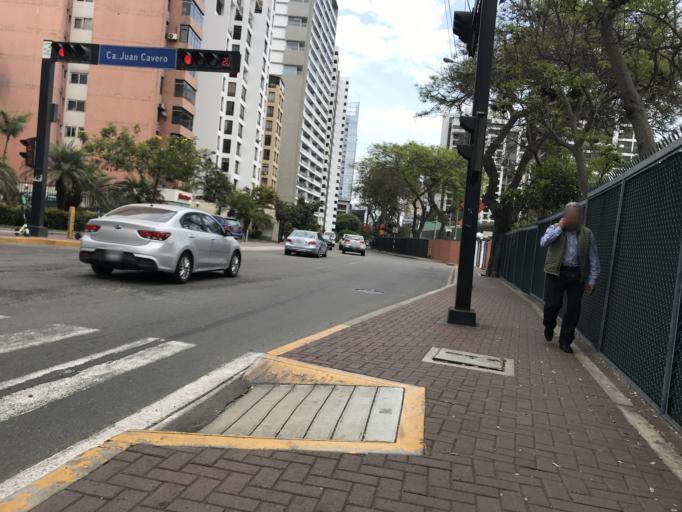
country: PE
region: Lima
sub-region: Lima
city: San Isidro
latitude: -12.1018
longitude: -77.0384
